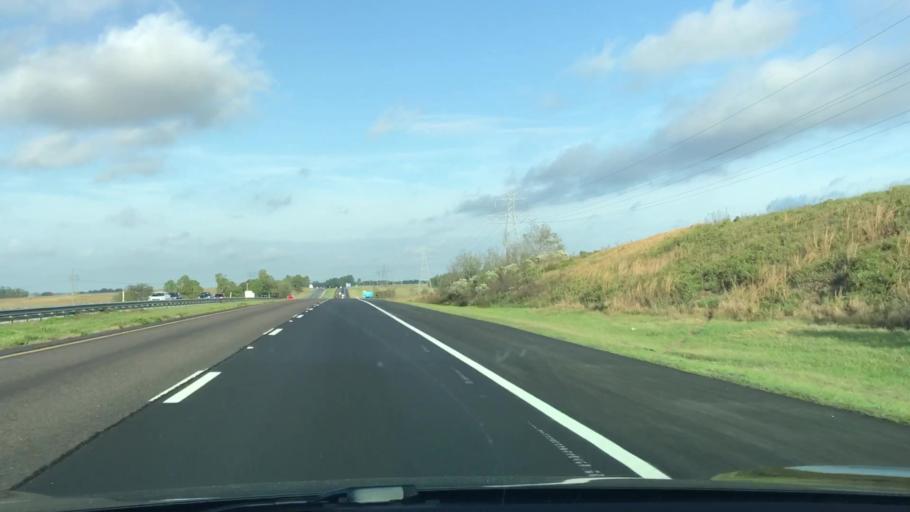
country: US
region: Florida
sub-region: Lake County
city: Hawthorne
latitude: 28.7641
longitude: -81.9475
